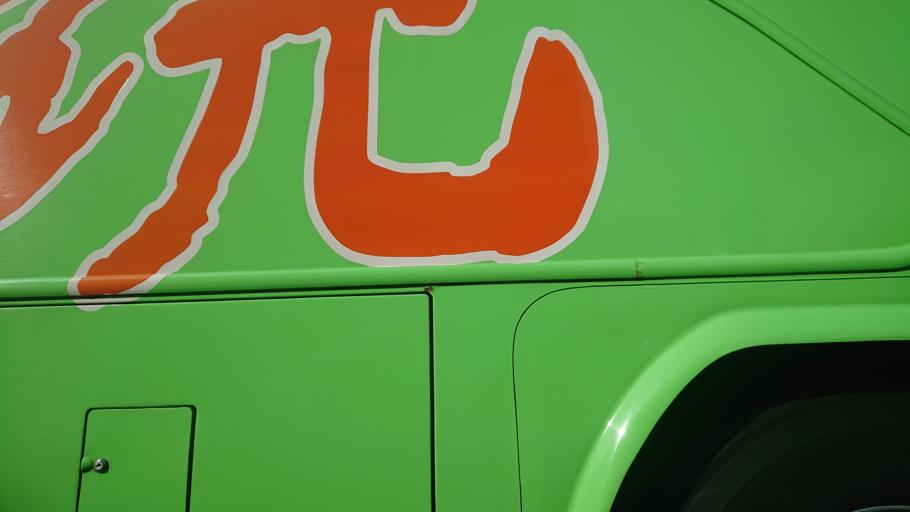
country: TW
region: Taiwan
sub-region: Tainan
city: Tainan
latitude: 23.0063
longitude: 120.1865
